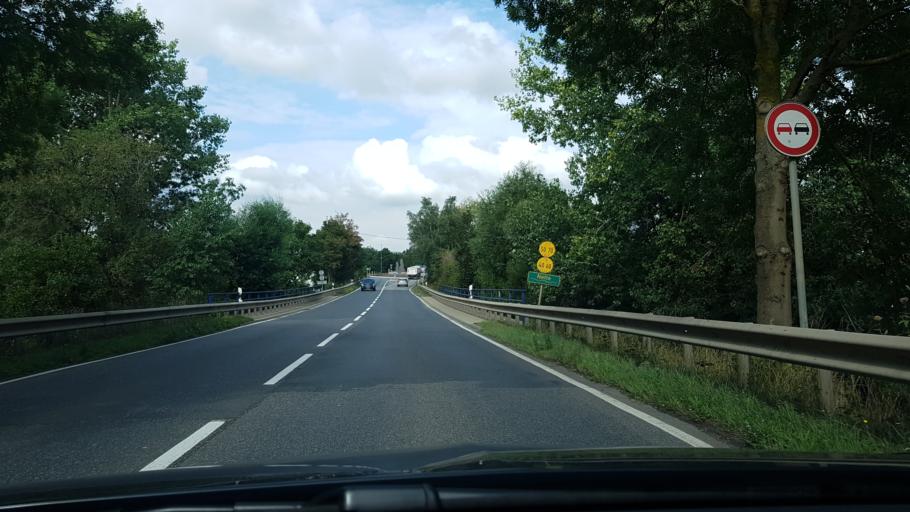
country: DE
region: Rheinland-Pfalz
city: Plaidt
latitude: 50.3867
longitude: 7.3852
